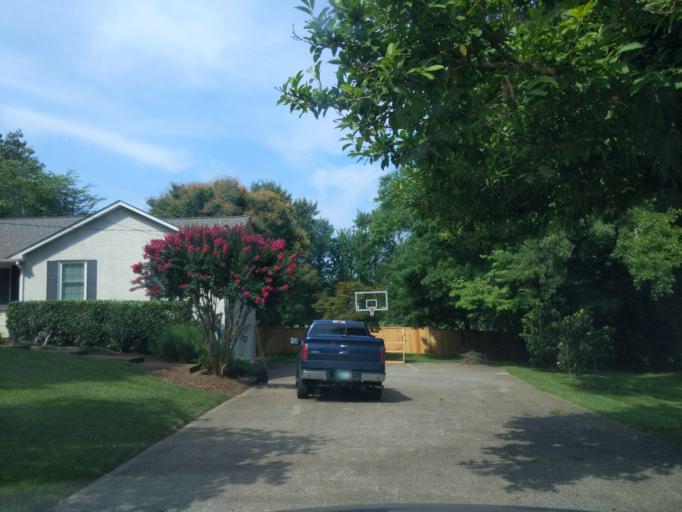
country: US
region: Tennessee
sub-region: Williamson County
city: Brentwood Estates
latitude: 36.0273
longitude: -86.7399
